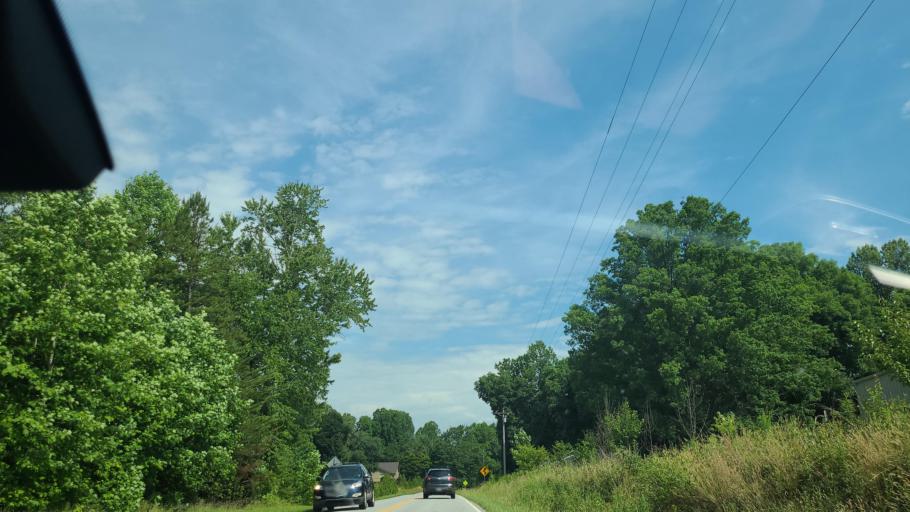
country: US
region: South Carolina
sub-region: Oconee County
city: Walhalla
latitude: 34.8209
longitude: -83.1284
